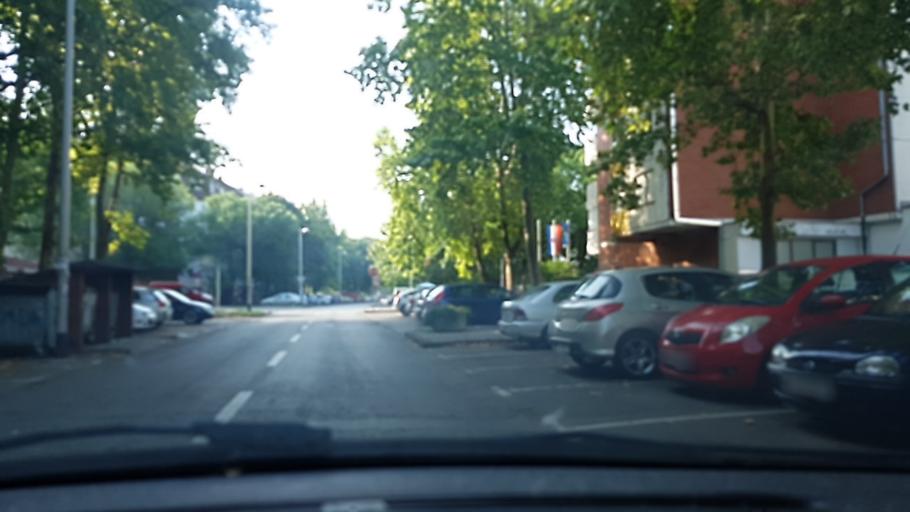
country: HR
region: Grad Zagreb
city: Jankomir
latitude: 45.7942
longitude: 15.9176
